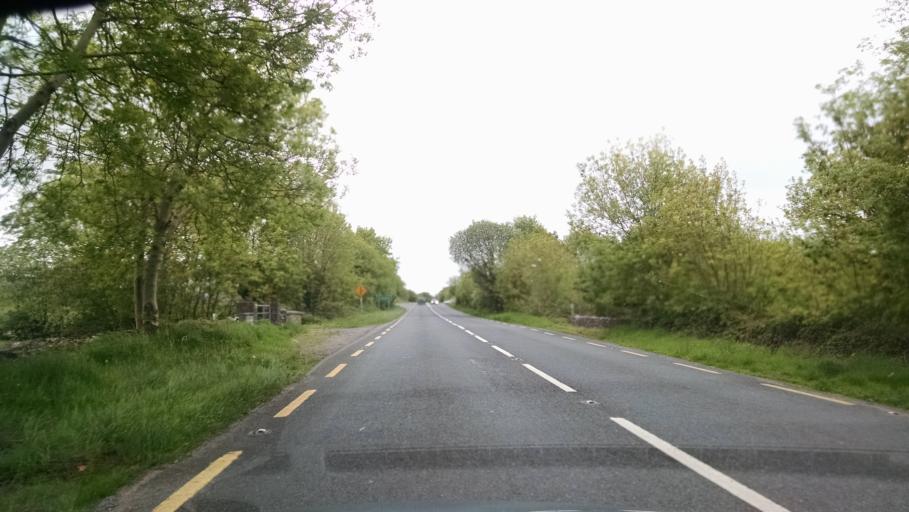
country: IE
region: Connaught
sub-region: County Galway
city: Claregalway
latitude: 53.4183
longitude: -9.0291
